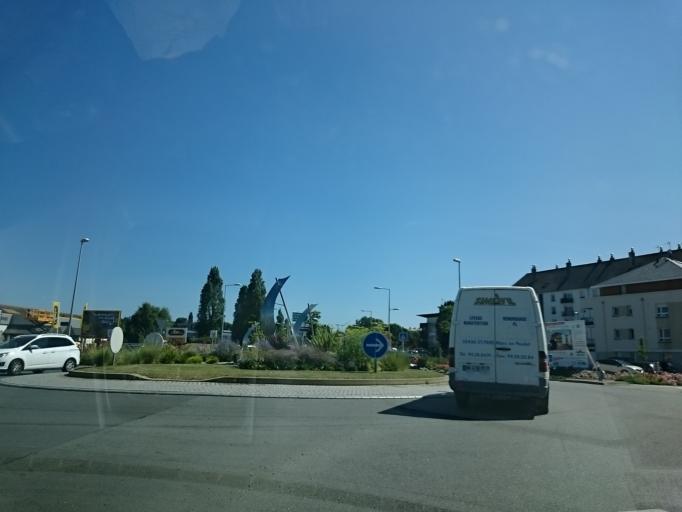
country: FR
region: Brittany
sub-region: Departement d'Ille-et-Vilaine
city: Saint-Malo
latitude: 48.6383
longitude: -1.9900
